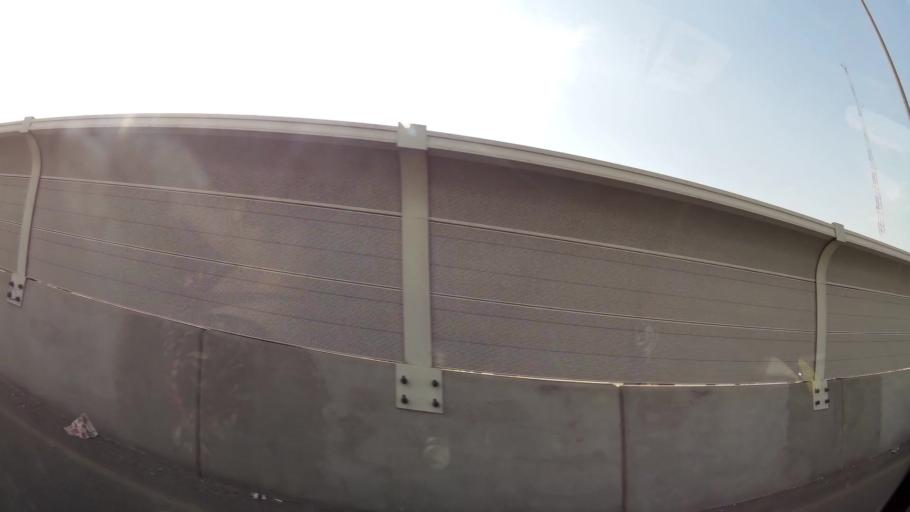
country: KW
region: Al Farwaniyah
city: Al Farwaniyah
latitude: 29.3083
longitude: 47.9773
